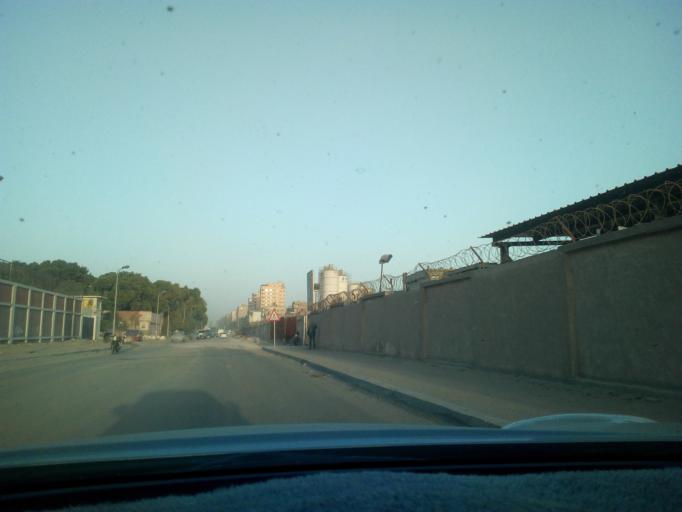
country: EG
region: Muhafazat al Qalyubiyah
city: Al Khankah
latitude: 30.1249
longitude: 31.3596
